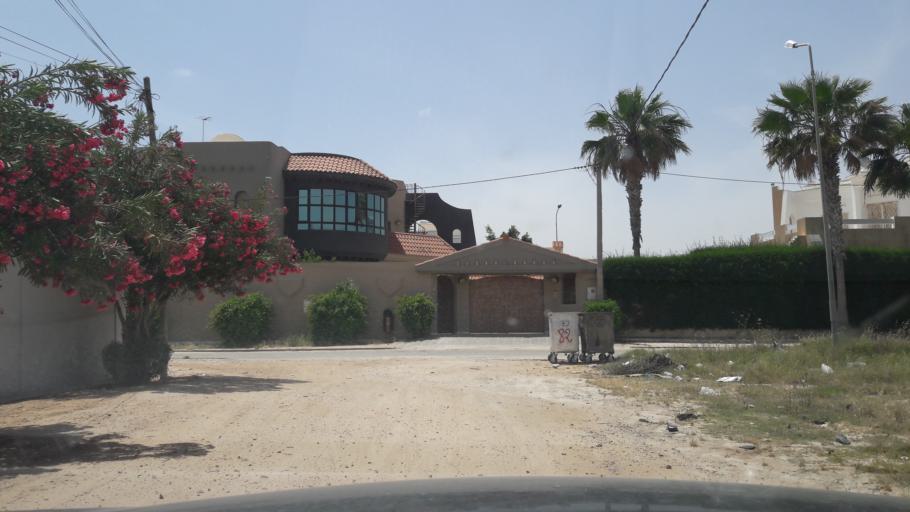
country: TN
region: Safaqis
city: Sfax
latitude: 34.7775
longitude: 10.7561
